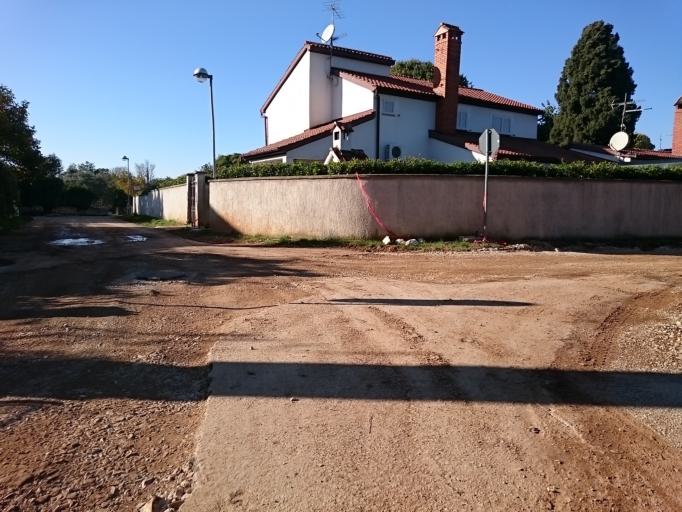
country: HR
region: Istarska
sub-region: Grad Porec
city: Porec
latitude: 45.2447
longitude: 13.6215
